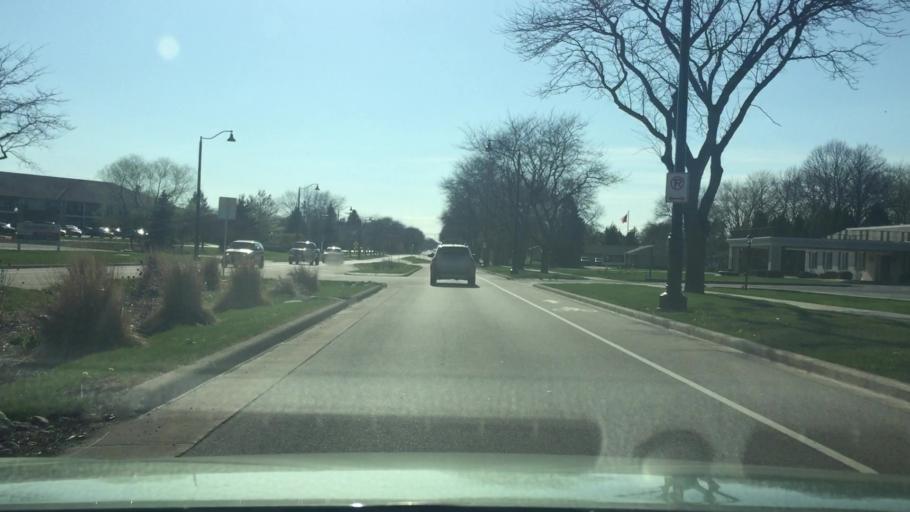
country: US
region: Wisconsin
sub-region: Milwaukee County
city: Brown Deer
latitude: 43.1632
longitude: -87.9715
